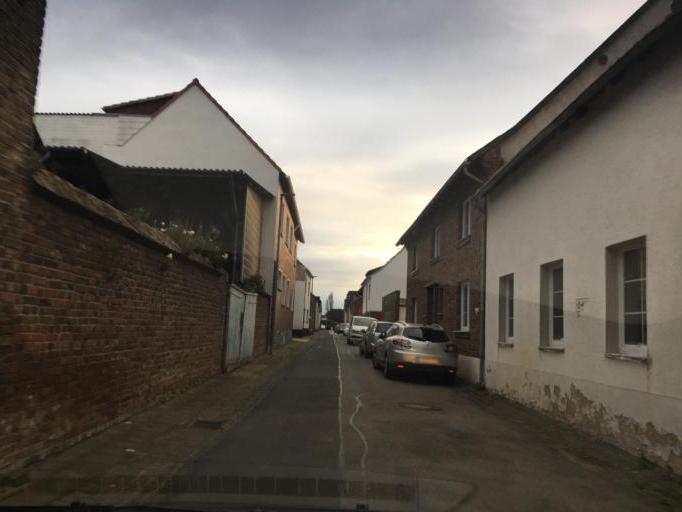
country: DE
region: North Rhine-Westphalia
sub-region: Regierungsbezirk Koln
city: Norvenich
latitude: 50.7662
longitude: 6.7215
